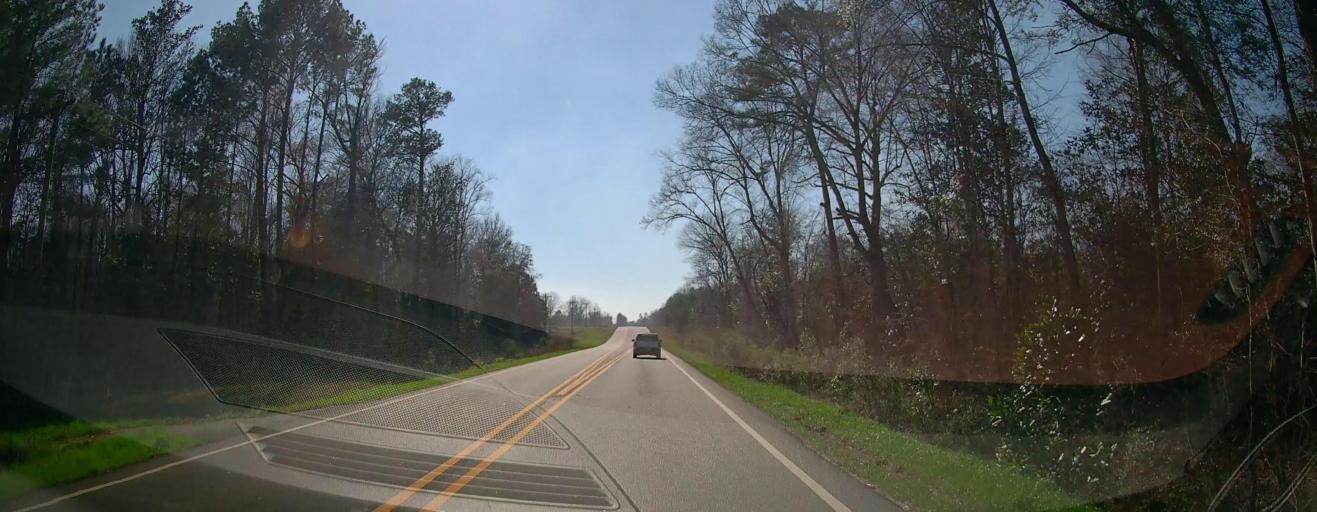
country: US
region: Georgia
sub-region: Macon County
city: Marshallville
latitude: 32.3251
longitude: -83.8792
